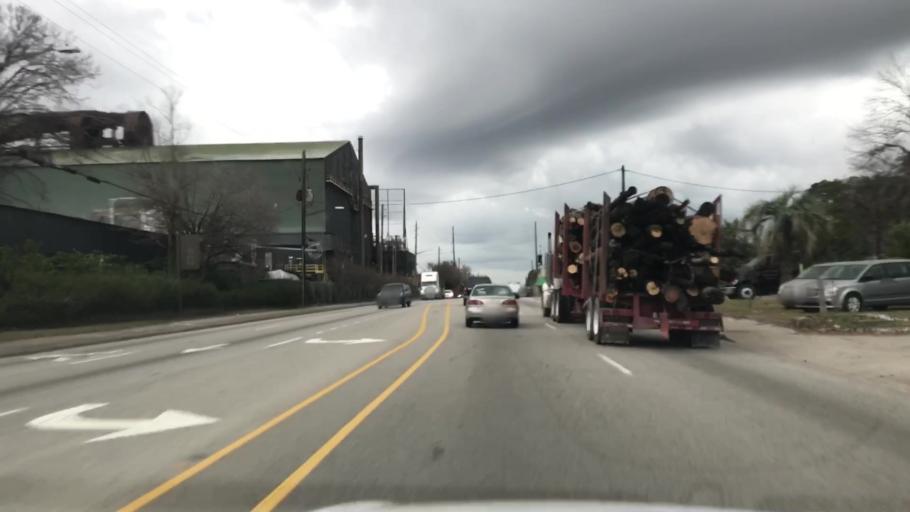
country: US
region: South Carolina
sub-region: Georgetown County
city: Georgetown
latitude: 33.3711
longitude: -79.2907
